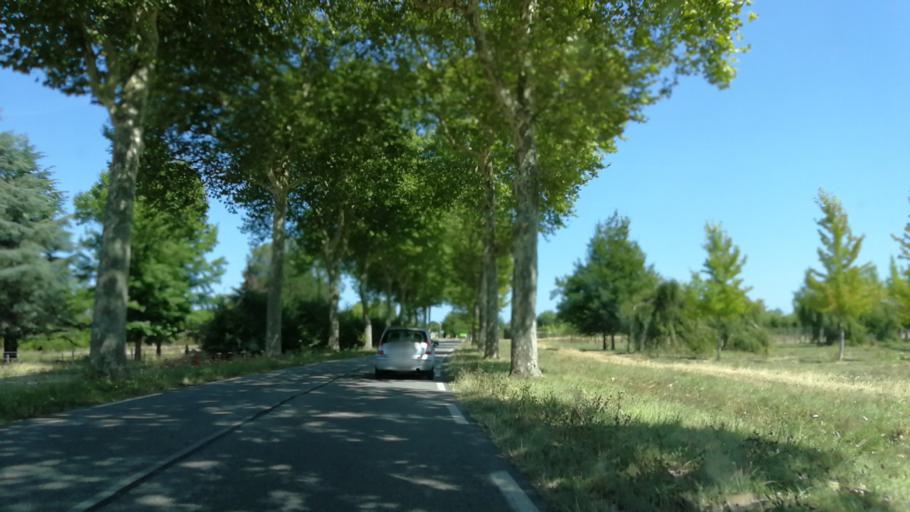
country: FR
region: Ile-de-France
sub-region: Departement des Yvelines
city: Dampierre-en-Yvelines
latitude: 48.6813
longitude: 1.9981
